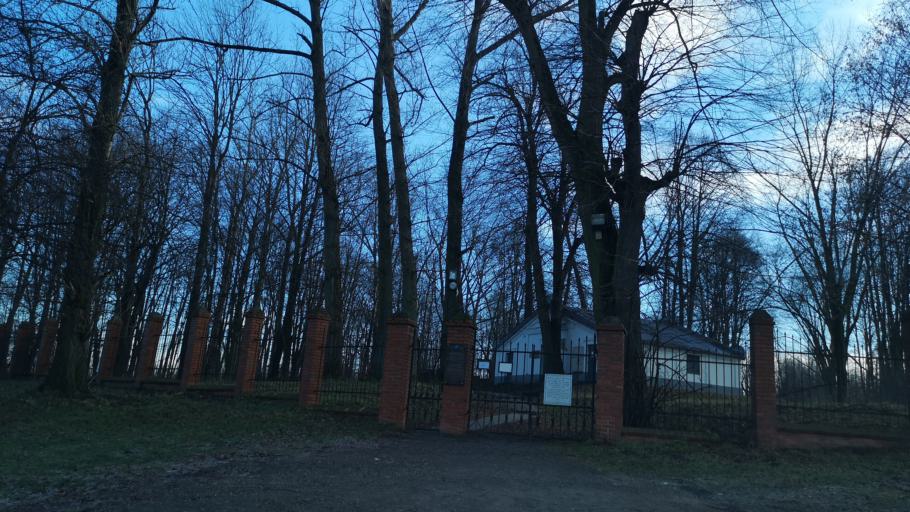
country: PL
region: Subcarpathian Voivodeship
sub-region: Powiat lezajski
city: Lezajsk
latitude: 50.2513
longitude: 22.4217
